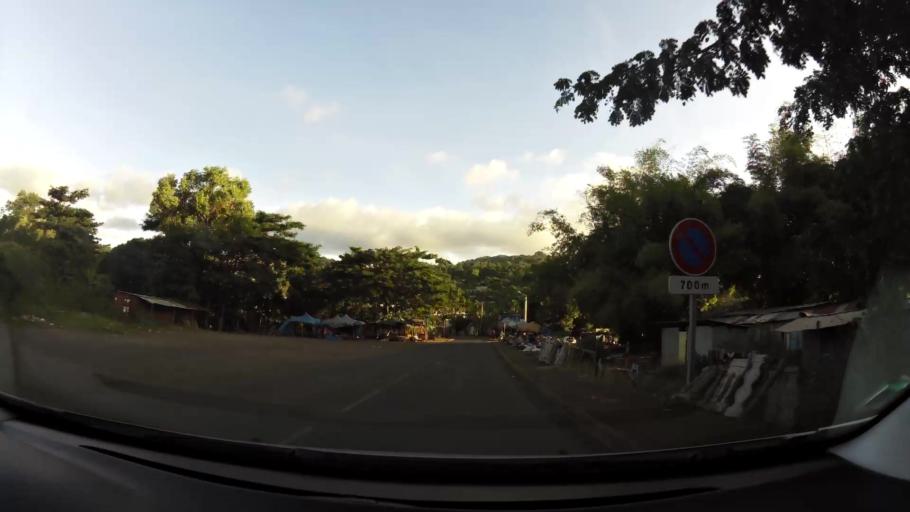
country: YT
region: Dembeni
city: Dembeni
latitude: -12.8418
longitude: 45.1842
